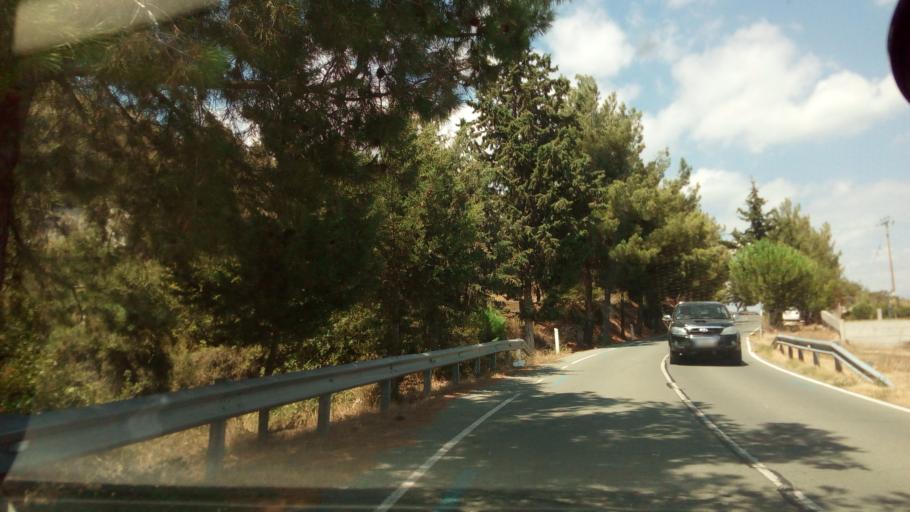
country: CY
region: Limassol
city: Pachna
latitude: 34.8381
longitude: 32.8578
